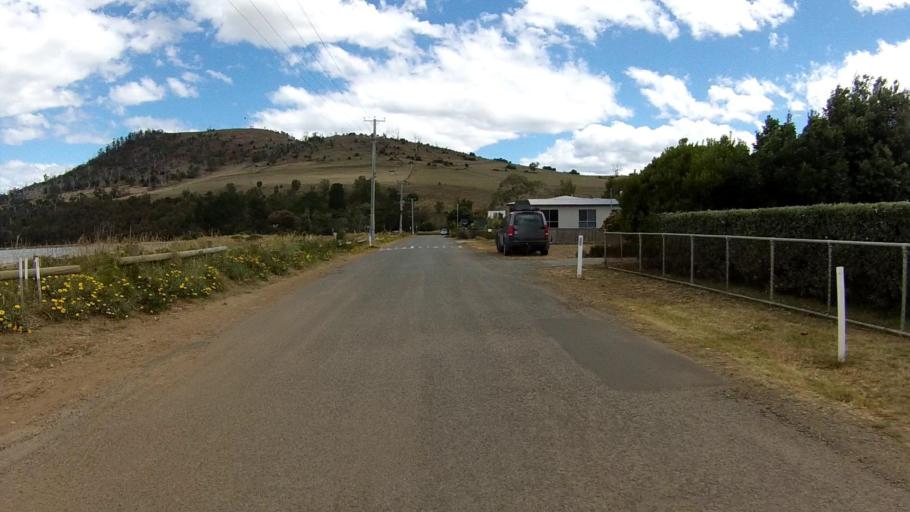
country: AU
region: Tasmania
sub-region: Clarence
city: Seven Mile Beach
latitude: -42.8641
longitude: 147.5033
